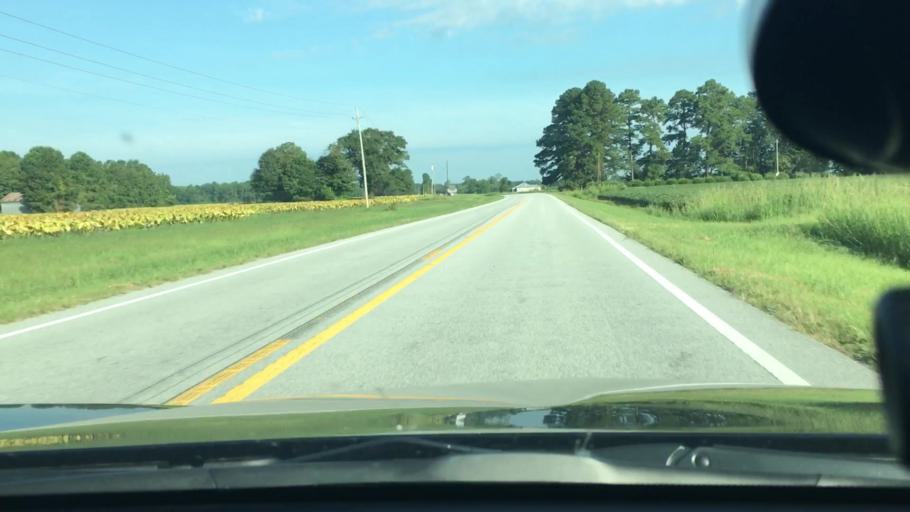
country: US
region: North Carolina
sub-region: Pitt County
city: Summerfield
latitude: 35.6670
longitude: -77.4784
